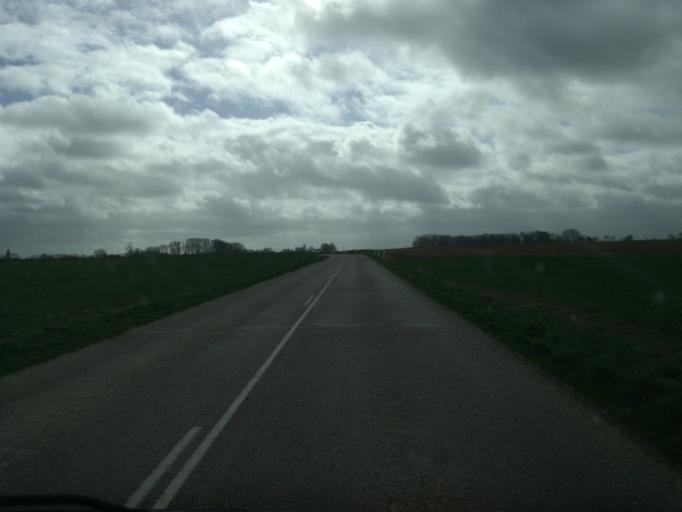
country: FR
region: Haute-Normandie
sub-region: Departement de la Seine-Maritime
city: Valliquerville
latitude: 49.6028
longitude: 0.6678
